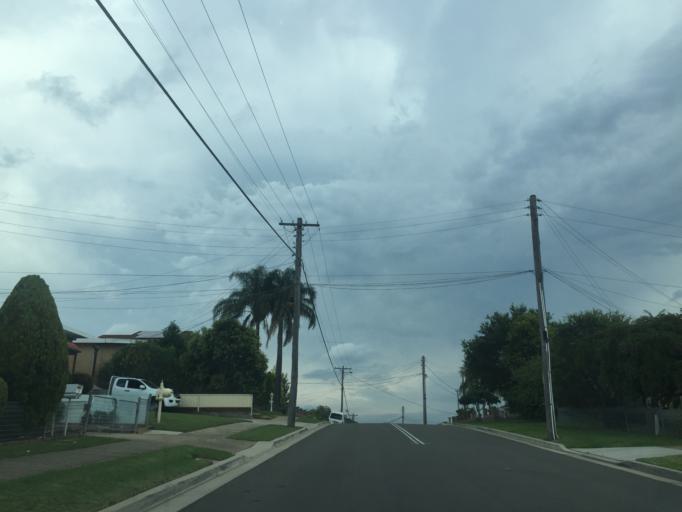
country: AU
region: New South Wales
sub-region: Blacktown
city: Blacktown
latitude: -33.7847
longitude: 150.8966
